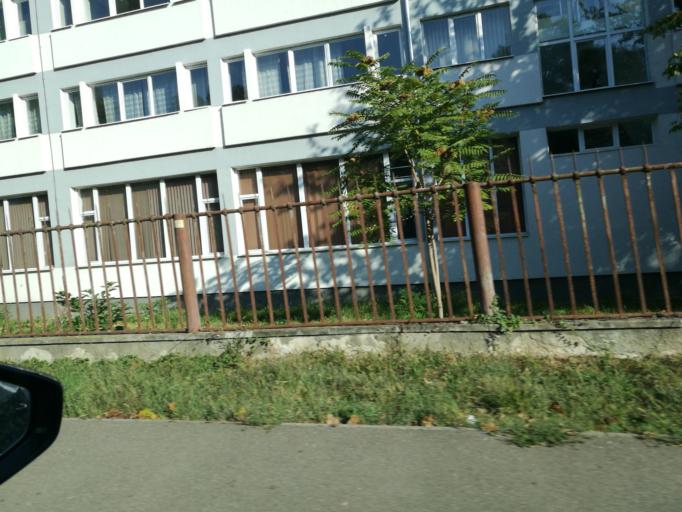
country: RO
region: Bihor
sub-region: Comuna Biharea
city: Oradea
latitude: 47.0422
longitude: 21.9186
